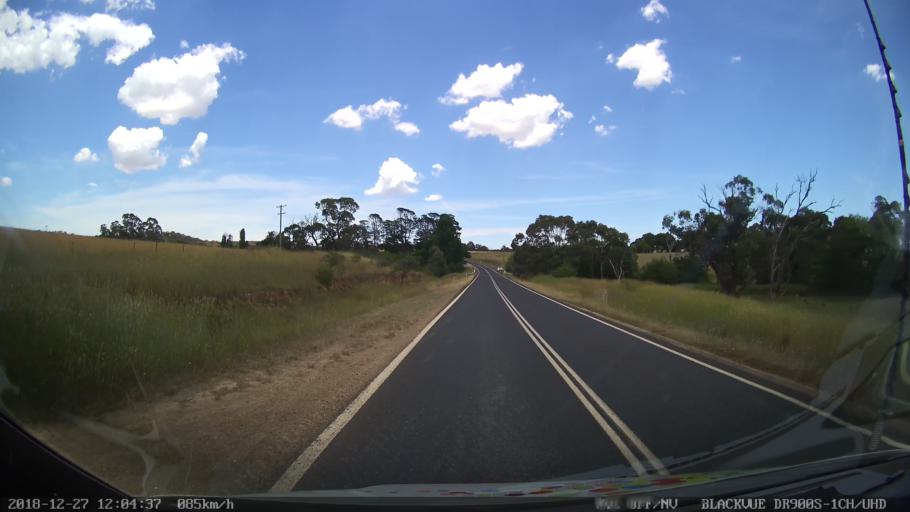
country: AU
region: New South Wales
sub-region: Blayney
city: Blayney
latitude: -33.7982
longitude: 149.3480
